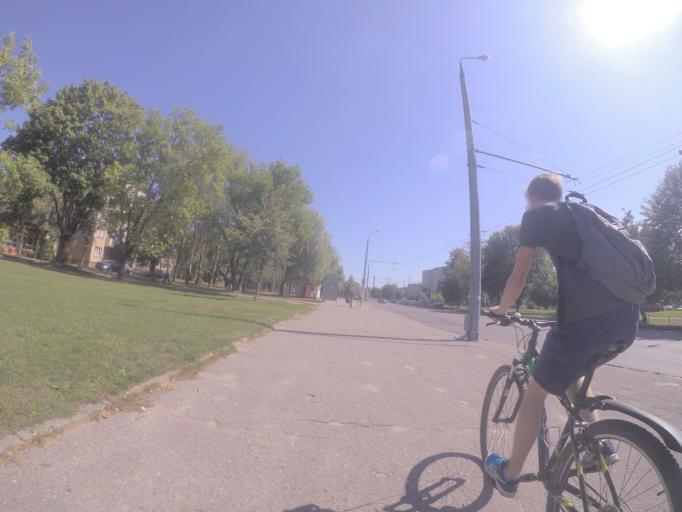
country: BY
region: Grodnenskaya
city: Hrodna
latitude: 53.6653
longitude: 23.7885
